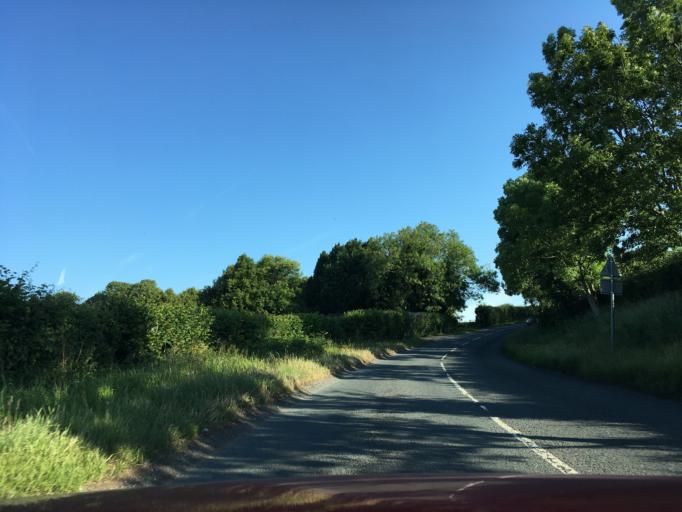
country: GB
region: Wales
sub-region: Monmouthshire
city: Tintern
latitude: 51.7190
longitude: -2.6350
